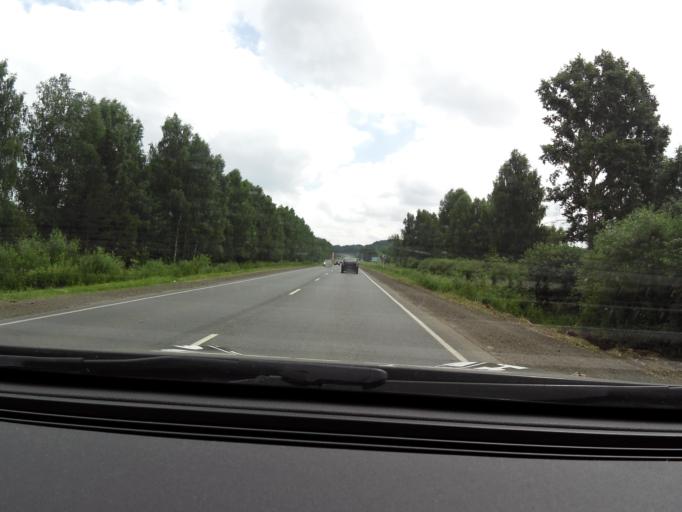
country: RU
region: Perm
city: Kungur
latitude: 57.4623
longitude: 56.7591
